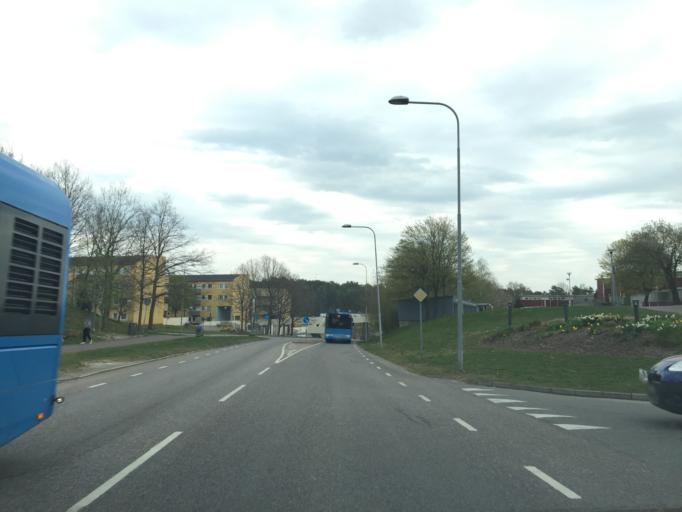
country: SE
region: Vaestra Goetaland
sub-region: Goteborg
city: Loevgaerdet
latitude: 57.8160
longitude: 12.0358
